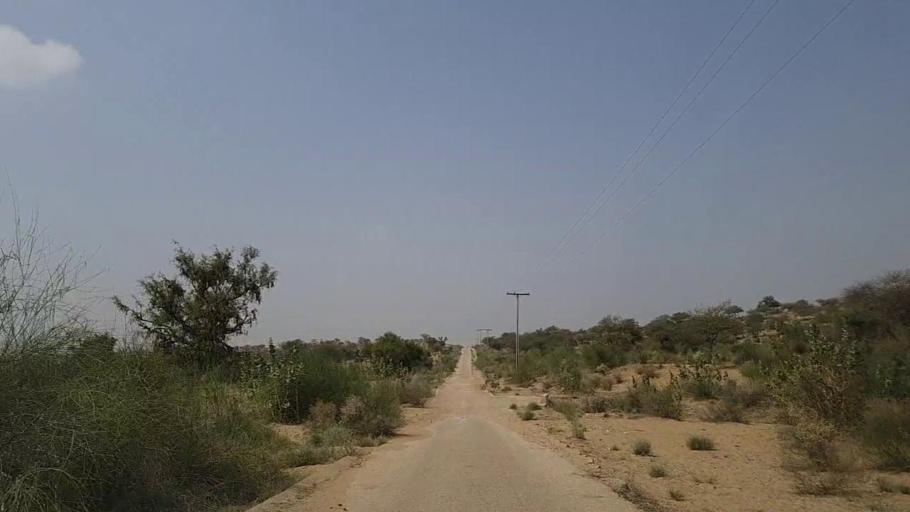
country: PK
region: Sindh
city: Mithi
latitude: 24.7676
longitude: 69.8952
